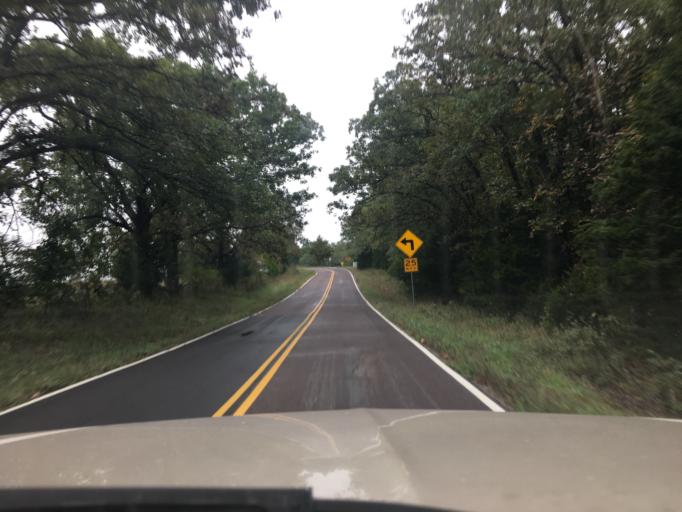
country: US
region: Missouri
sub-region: Crawford County
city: Cuba
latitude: 38.1839
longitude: -91.4861
